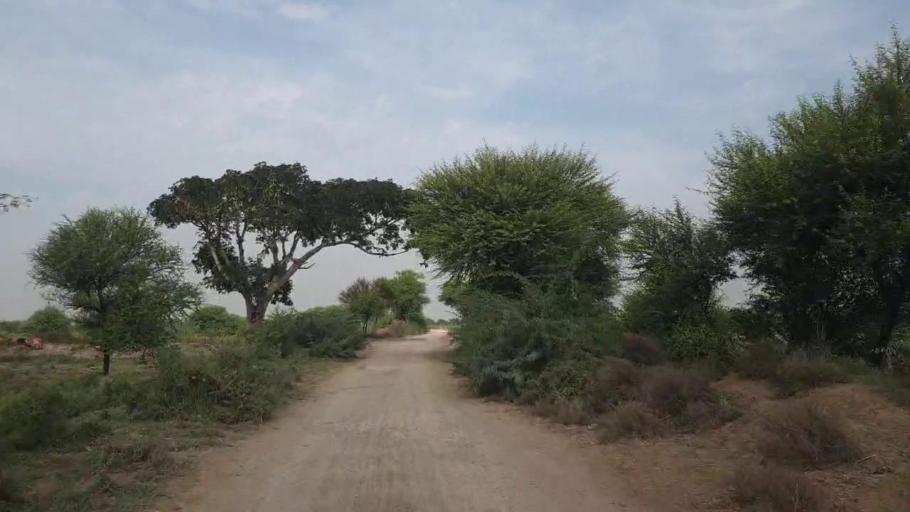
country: PK
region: Sindh
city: Rajo Khanani
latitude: 24.9713
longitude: 68.9962
